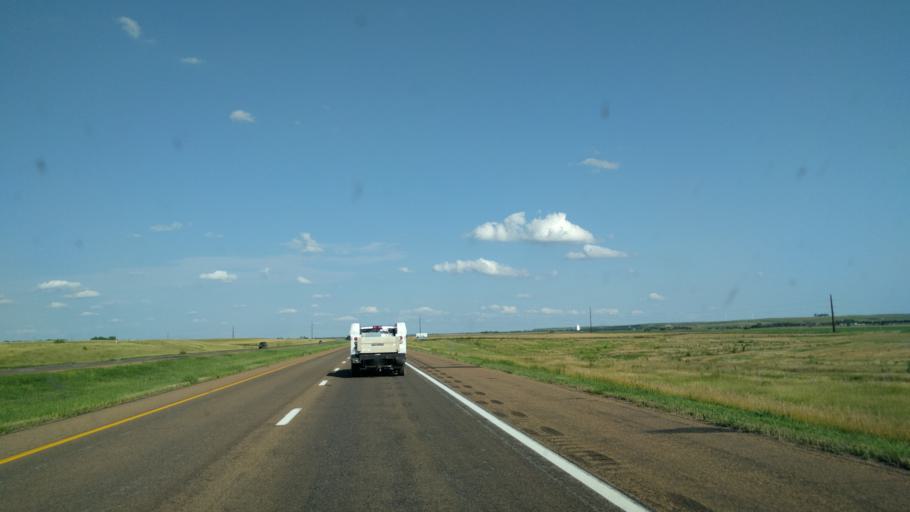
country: US
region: Kansas
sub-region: Ellis County
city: Ellis
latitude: 38.9350
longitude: -99.4712
